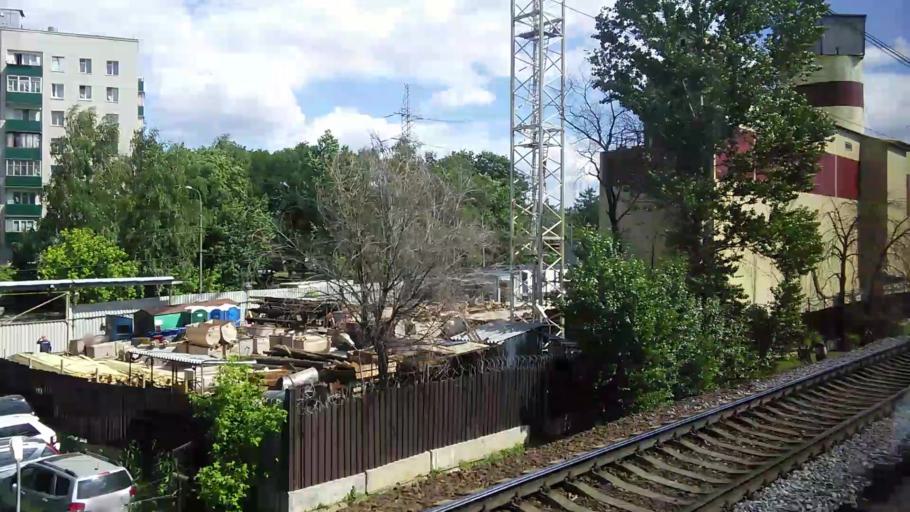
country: RU
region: Moscow
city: Novovladykino
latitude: 55.8414
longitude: 37.5780
